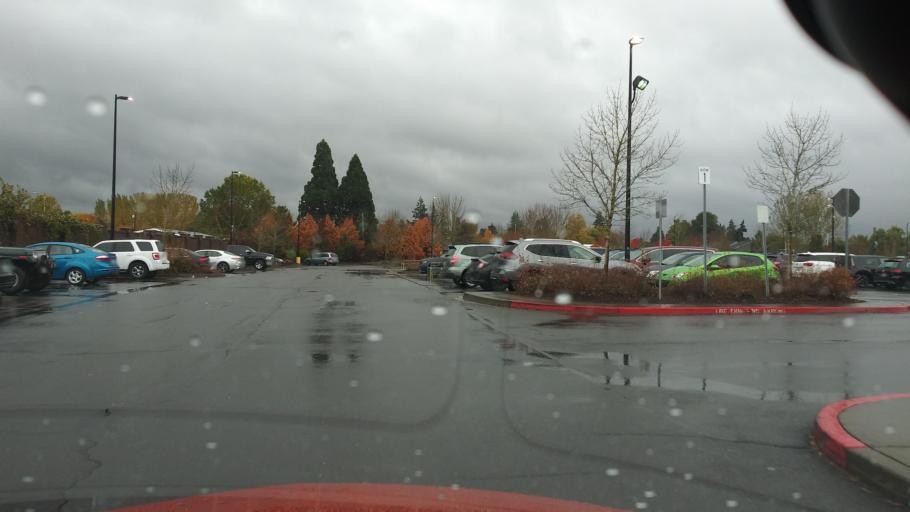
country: US
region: Oregon
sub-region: Washington County
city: Cornelius
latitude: 45.5229
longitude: -123.0690
